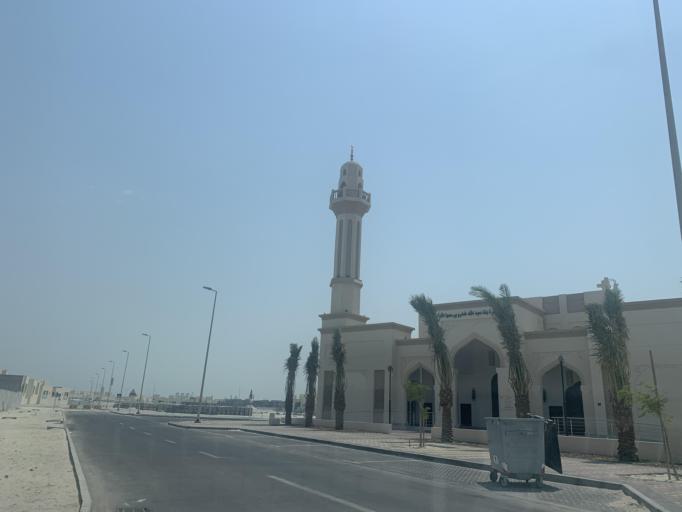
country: BH
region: Muharraq
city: Al Hadd
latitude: 26.2441
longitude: 50.6675
